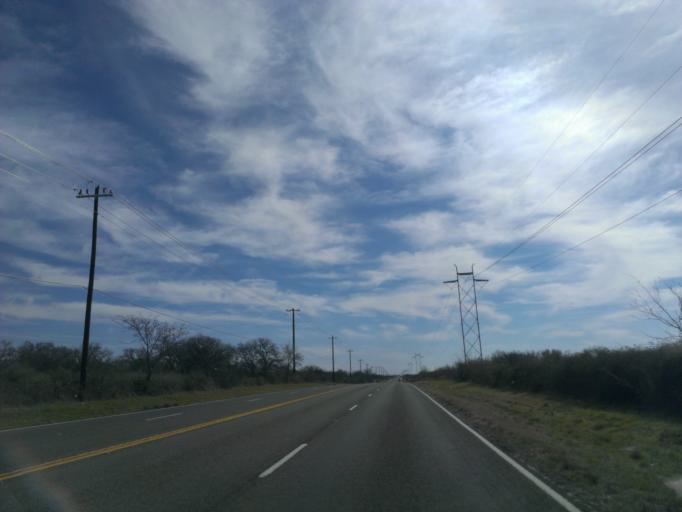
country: US
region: Texas
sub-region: Burnet County
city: Granite Shoals
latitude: 30.6248
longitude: -98.4028
